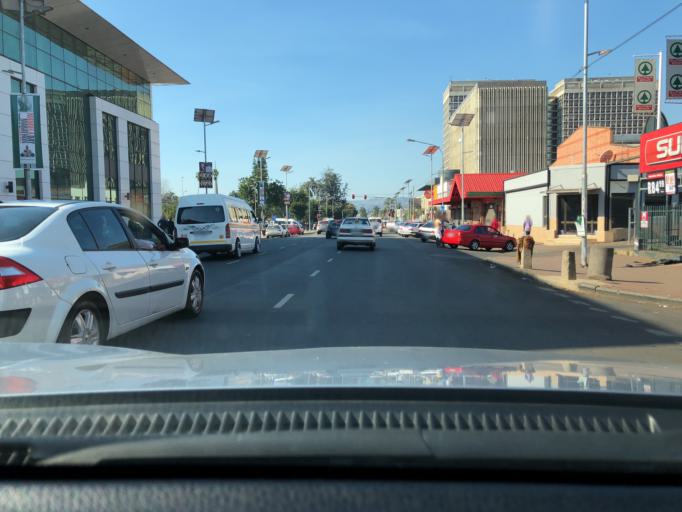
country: ZA
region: KwaZulu-Natal
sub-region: uMgungundlovu District Municipality
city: Pietermaritzburg
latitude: -29.6023
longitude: 30.3808
